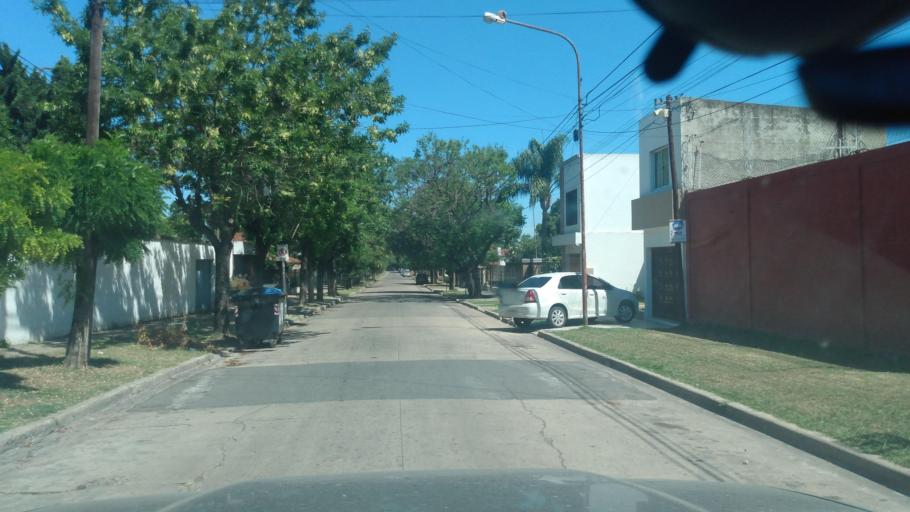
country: AR
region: Buenos Aires
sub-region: Partido de Lujan
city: Lujan
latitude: -34.5598
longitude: -59.1032
